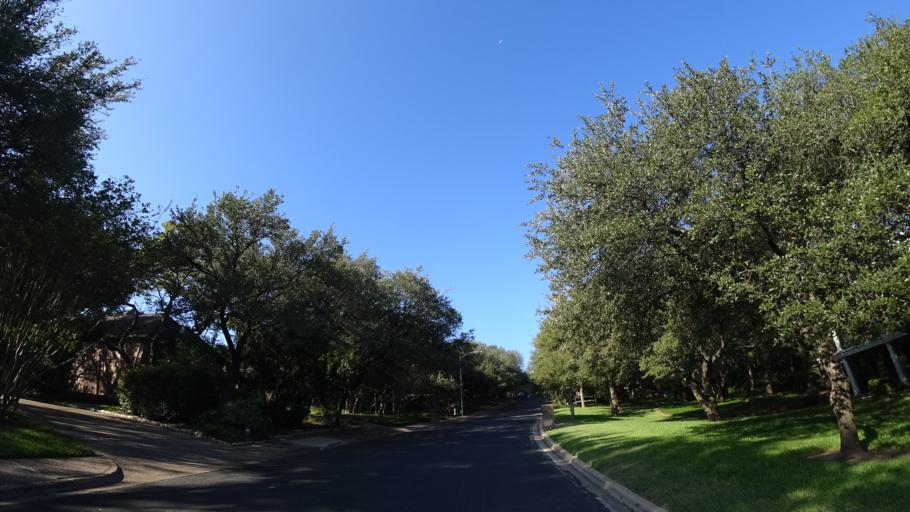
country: US
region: Texas
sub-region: Travis County
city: Rollingwood
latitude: 30.2650
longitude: -97.7937
